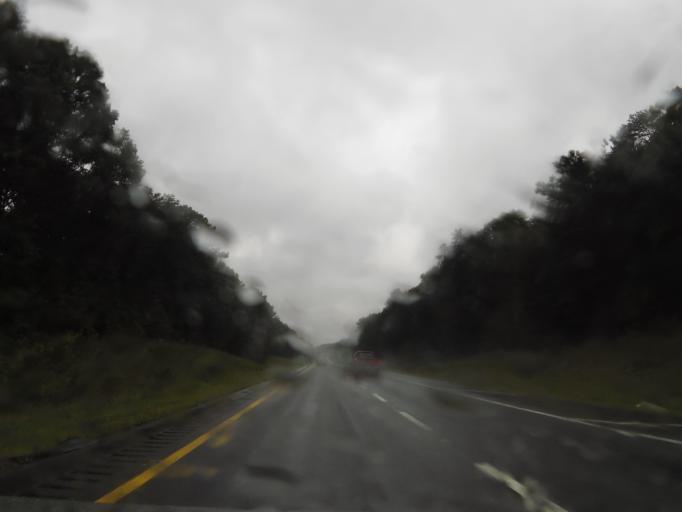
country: US
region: Tennessee
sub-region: Bradley County
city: Hopewell
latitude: 35.2652
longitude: -84.8303
